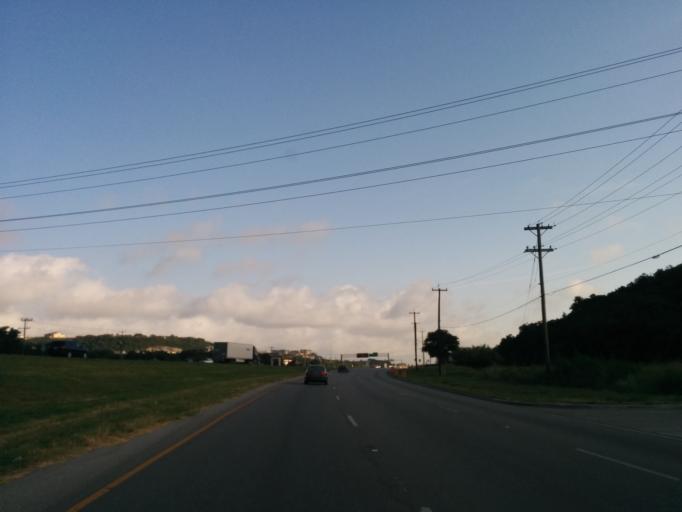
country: US
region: Texas
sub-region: Bexar County
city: Cross Mountain
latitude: 29.6166
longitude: -98.6063
